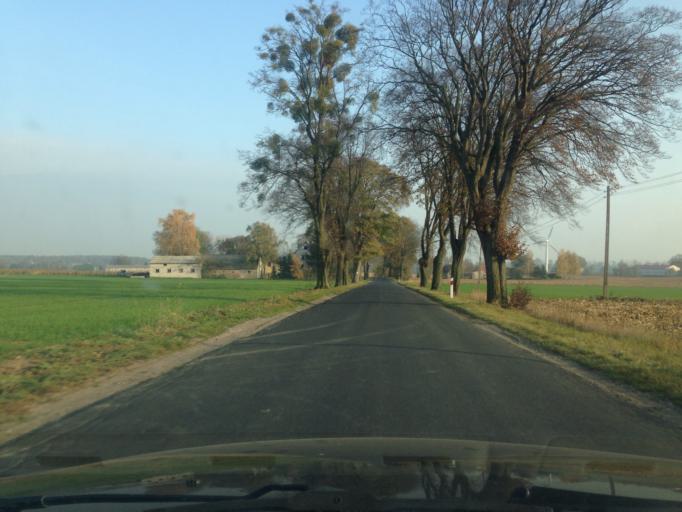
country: PL
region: Kujawsko-Pomorskie
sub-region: Powiat wabrzeski
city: Debowa Laka
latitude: 53.2335
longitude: 19.1732
